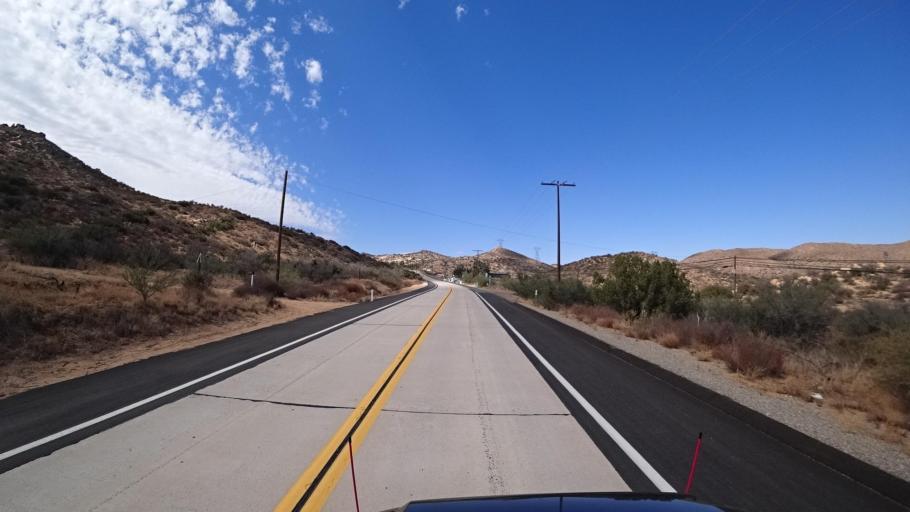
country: MX
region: Baja California
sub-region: Tecate
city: Cereso del Hongo
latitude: 32.6384
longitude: -116.2279
